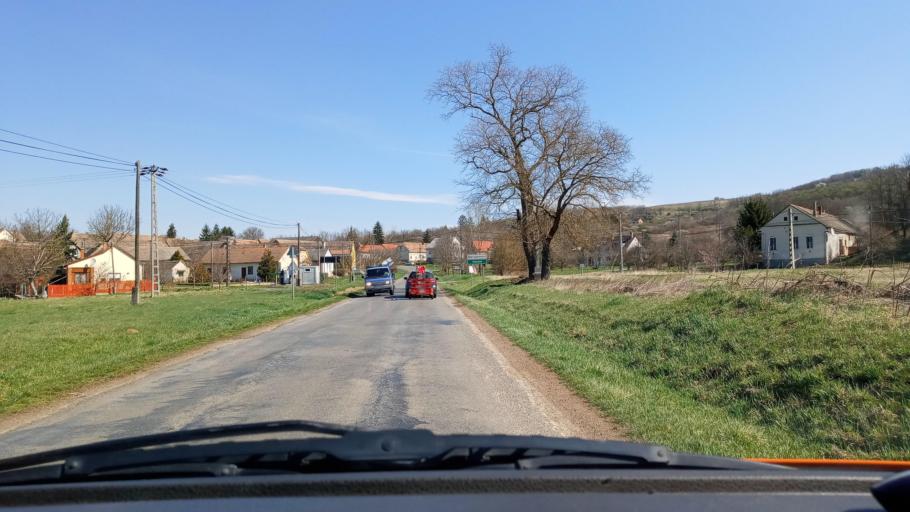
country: HU
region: Baranya
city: Boly
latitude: 46.0231
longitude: 18.4609
